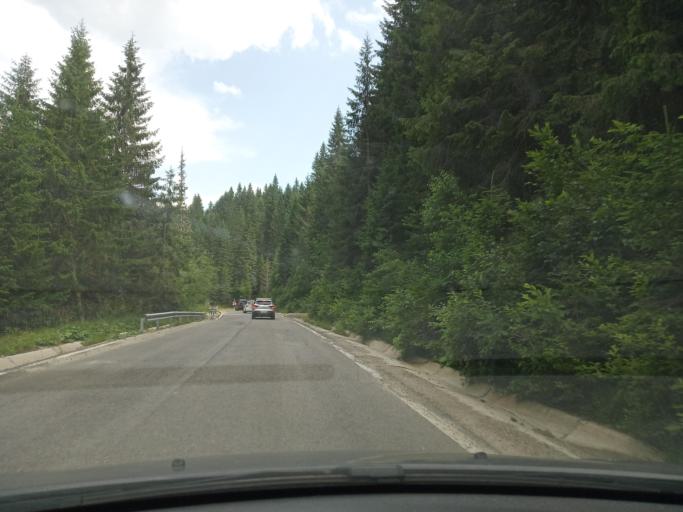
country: RO
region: Dambovita
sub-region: Comuna Moroeni
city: Glod
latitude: 45.3290
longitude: 25.4307
